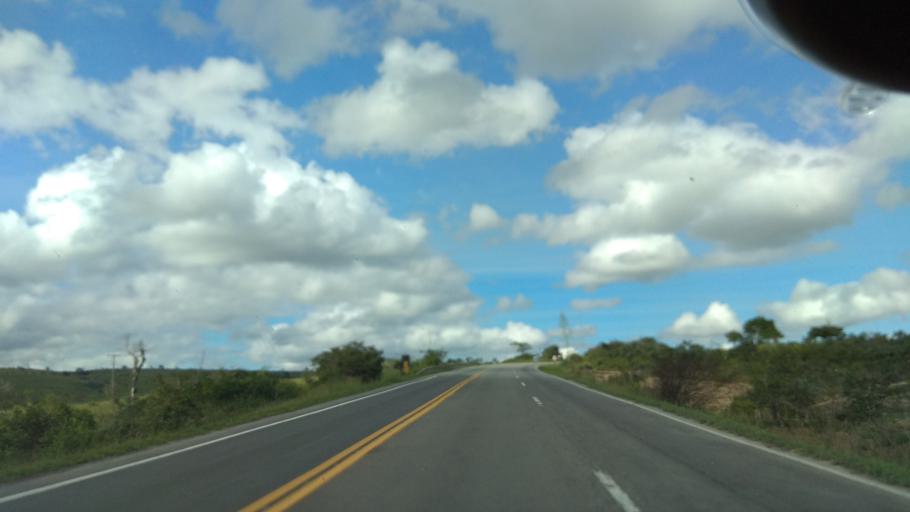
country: BR
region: Bahia
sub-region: Santa Ines
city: Santa Ines
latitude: -13.1052
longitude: -39.9823
